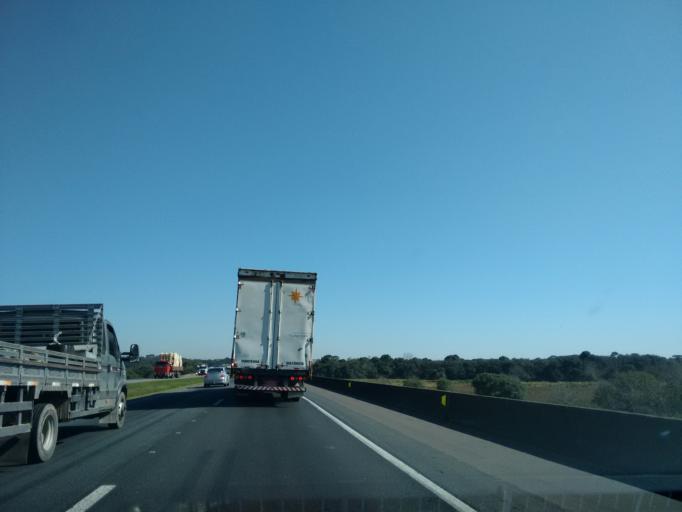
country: BR
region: Parana
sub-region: Sao Jose Dos Pinhais
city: Sao Jose dos Pinhais
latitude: -25.5674
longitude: -49.2367
